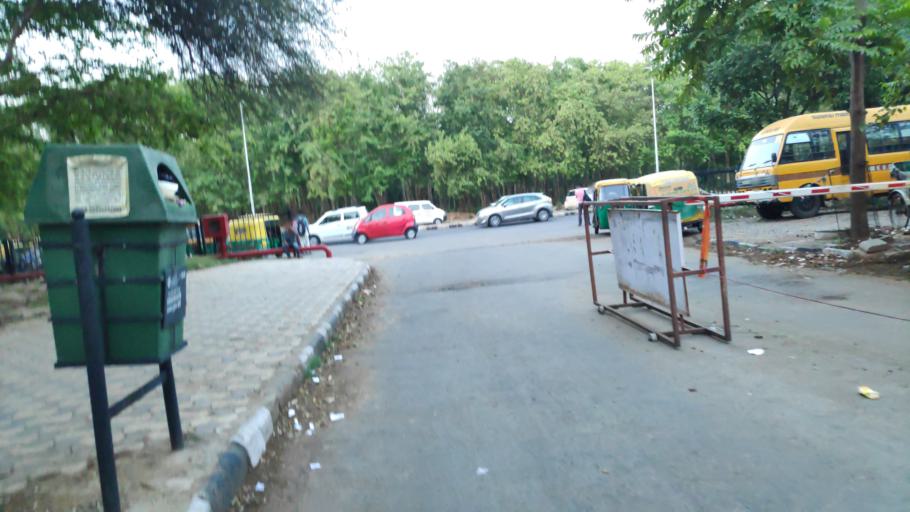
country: IN
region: Punjab
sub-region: Ajitgarh
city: Mohali
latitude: 30.7176
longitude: 76.7444
